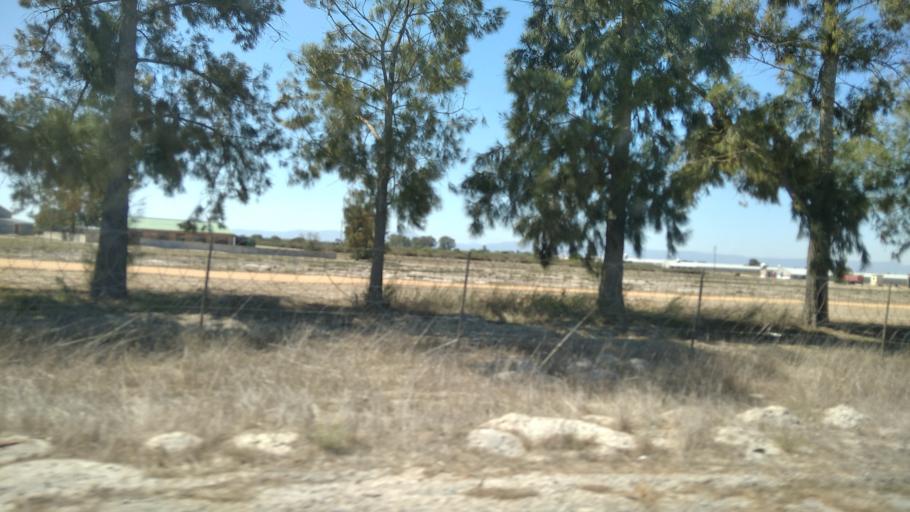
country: ZA
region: Western Cape
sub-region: West Coast District Municipality
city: Vredenburg
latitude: -33.0372
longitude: 18.3025
